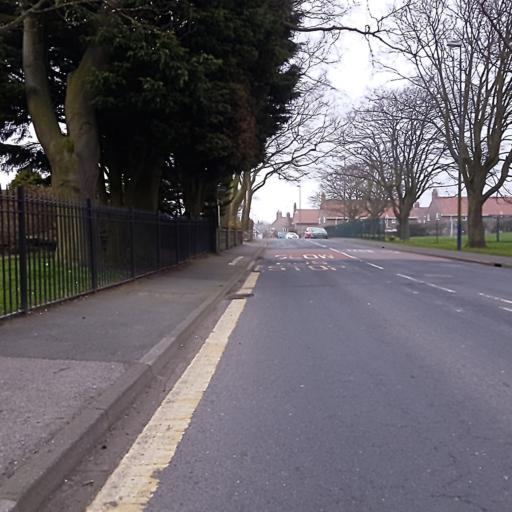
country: GB
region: England
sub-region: North Yorkshire
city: Filey
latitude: 54.2138
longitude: -0.2953
